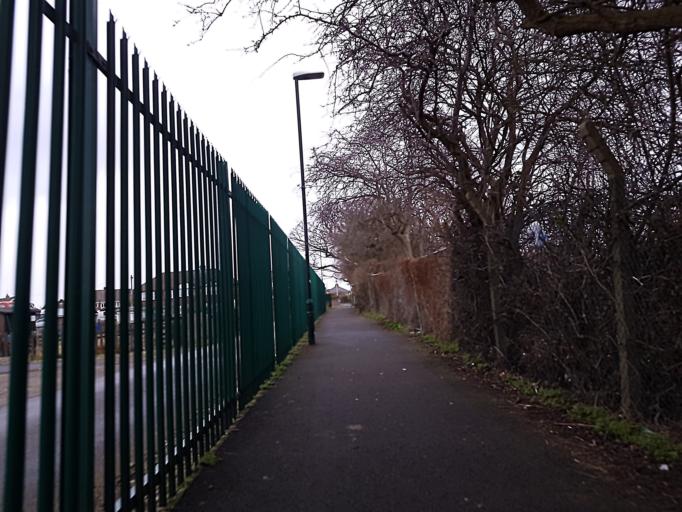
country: GB
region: England
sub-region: North East Lincolnshire
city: Grimbsy
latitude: 53.5608
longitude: -0.1028
